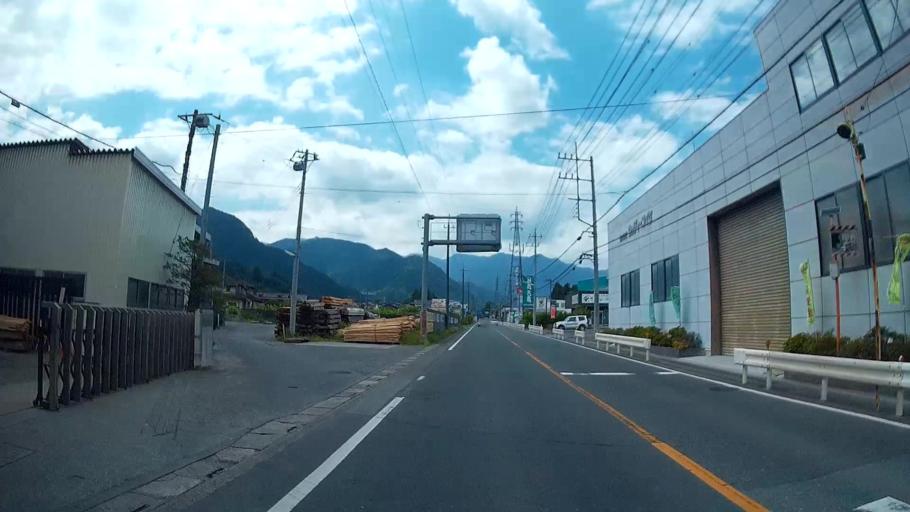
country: JP
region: Saitama
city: Chichibu
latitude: 35.9720
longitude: 139.0652
